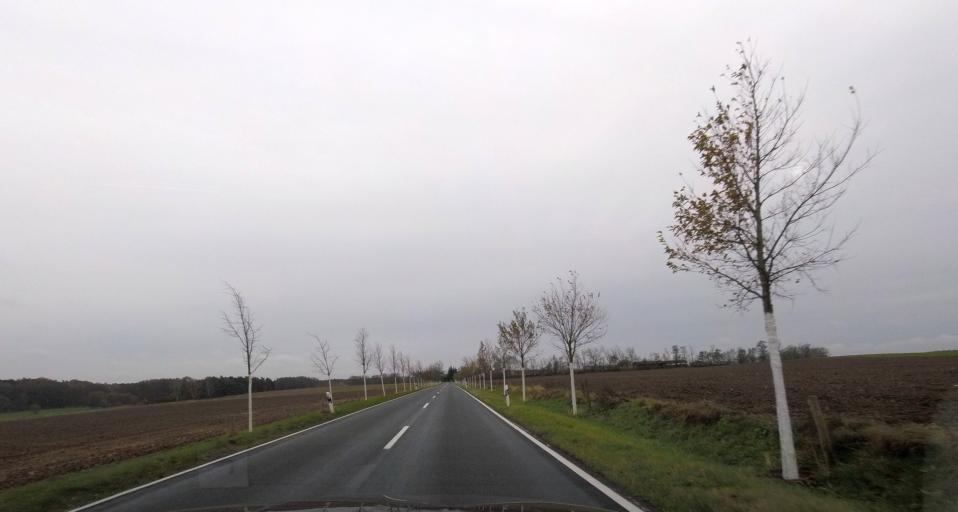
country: DE
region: Brandenburg
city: Niemegk
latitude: 52.0549
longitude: 12.6981
